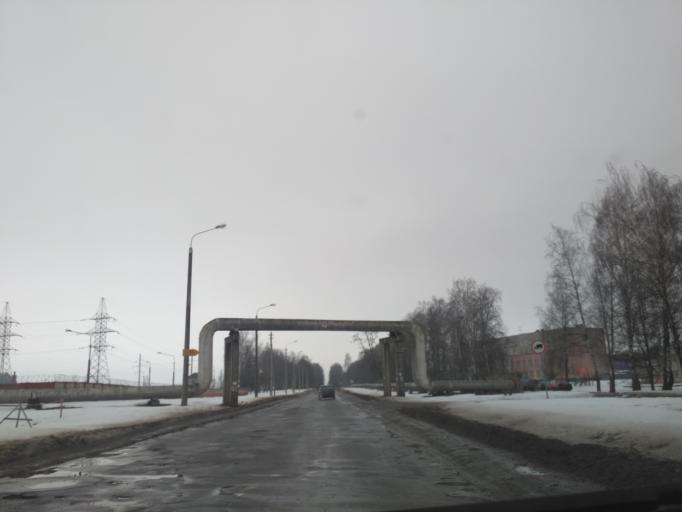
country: BY
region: Minsk
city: Horad Zhodzina
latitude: 54.0923
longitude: 28.3306
